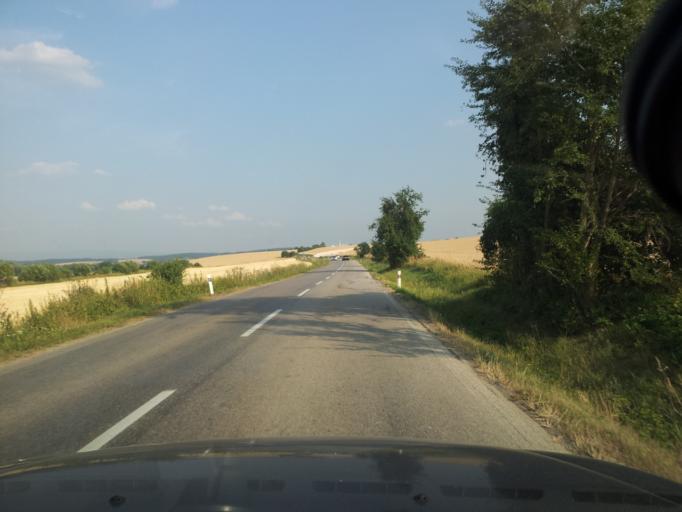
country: SK
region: Nitriansky
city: Banovce nad Bebravou
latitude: 48.7493
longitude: 18.2207
